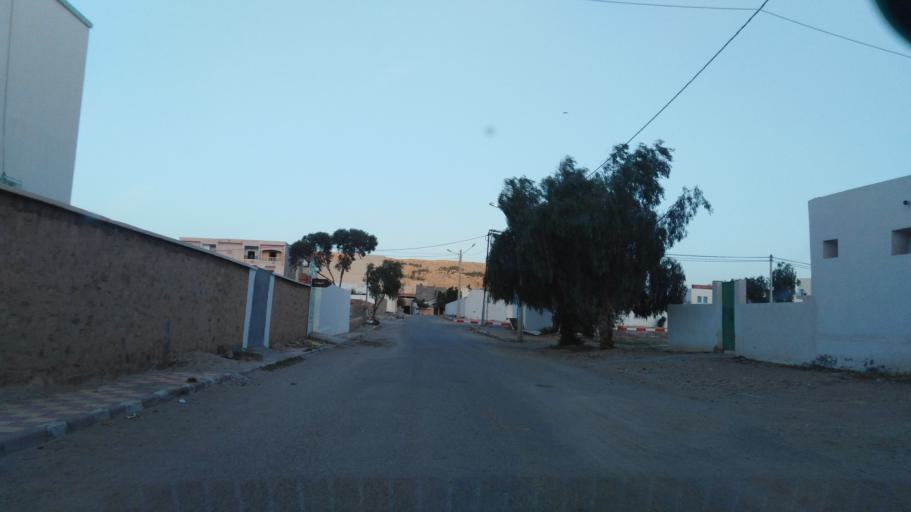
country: TN
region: Tataouine
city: Tataouine
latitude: 32.9406
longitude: 10.4538
